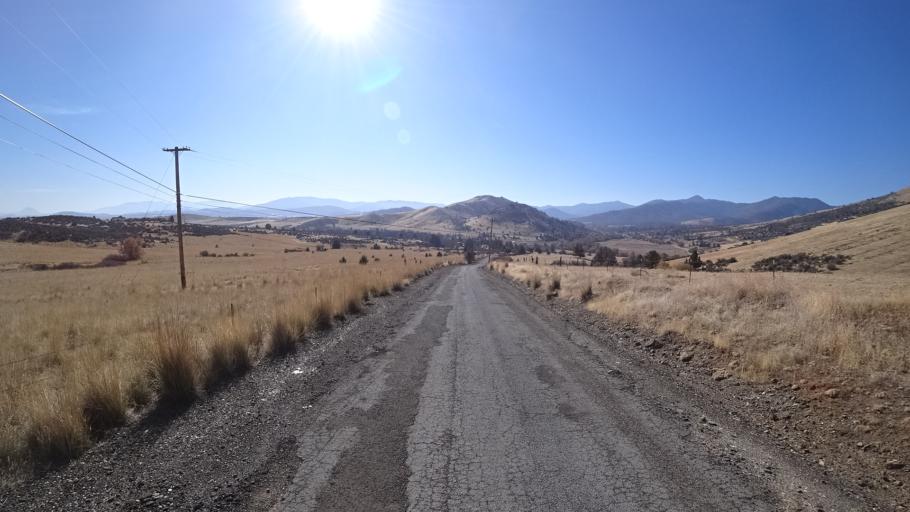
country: US
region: California
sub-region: Siskiyou County
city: Yreka
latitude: 41.7798
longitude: -122.5866
